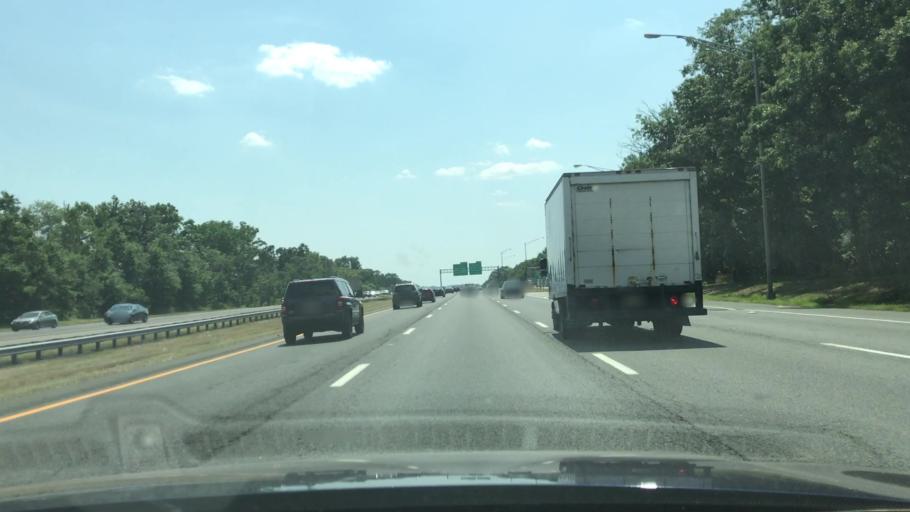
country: US
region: New Jersey
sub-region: Middlesex County
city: Middlesex
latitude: 40.5493
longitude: -74.4929
